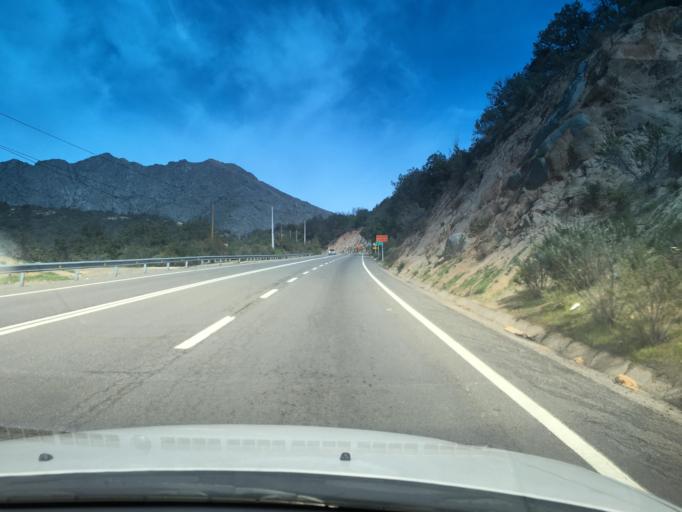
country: CL
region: Valparaiso
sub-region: Provincia de San Felipe
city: Llaillay
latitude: -33.0586
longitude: -71.0066
